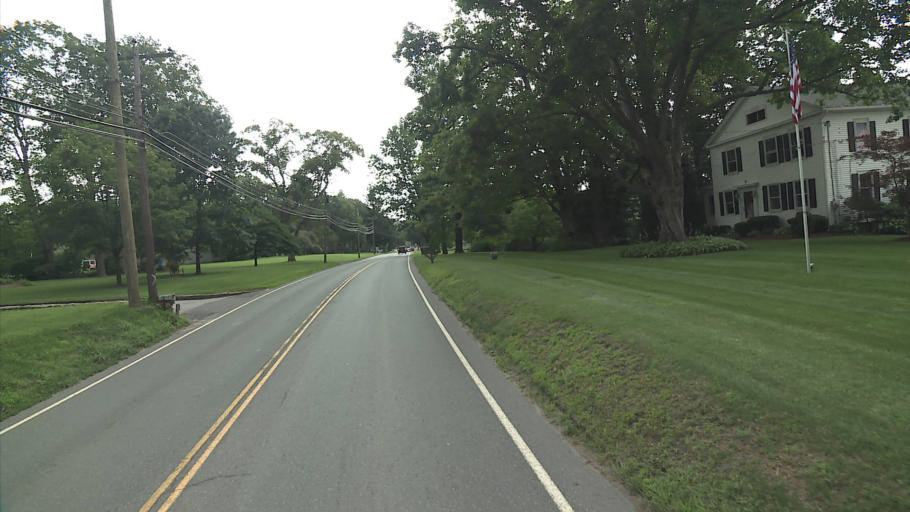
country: US
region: Connecticut
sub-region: New Haven County
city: Southbury
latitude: 41.4856
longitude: -73.2127
